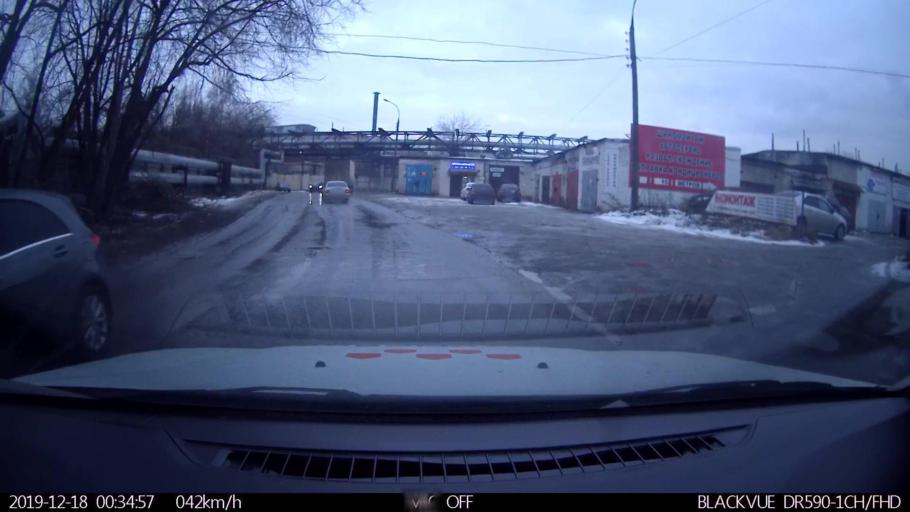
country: RU
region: Nizjnij Novgorod
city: Neklyudovo
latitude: 56.3528
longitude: 43.8784
